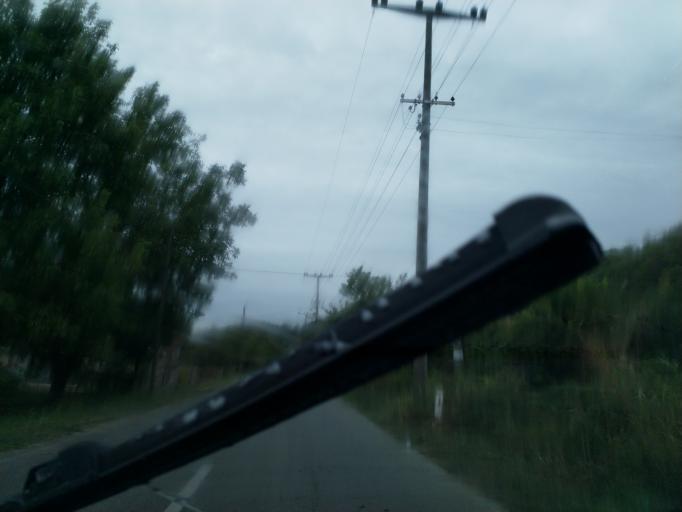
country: RS
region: Central Serbia
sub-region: Sumadijski Okrug
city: Batocina
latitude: 44.0996
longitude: 21.1636
